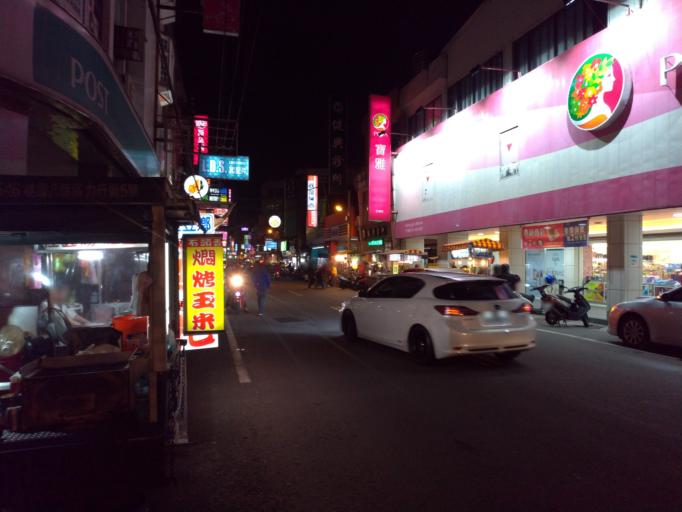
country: TW
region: Taiwan
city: Taoyuan City
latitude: 24.9744
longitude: 121.2560
